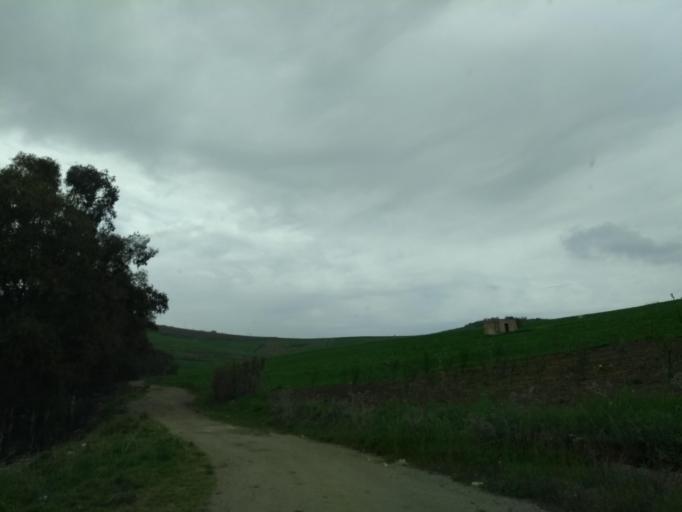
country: IT
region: Sicily
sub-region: Palermo
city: Partinico
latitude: 37.9892
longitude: 13.0823
